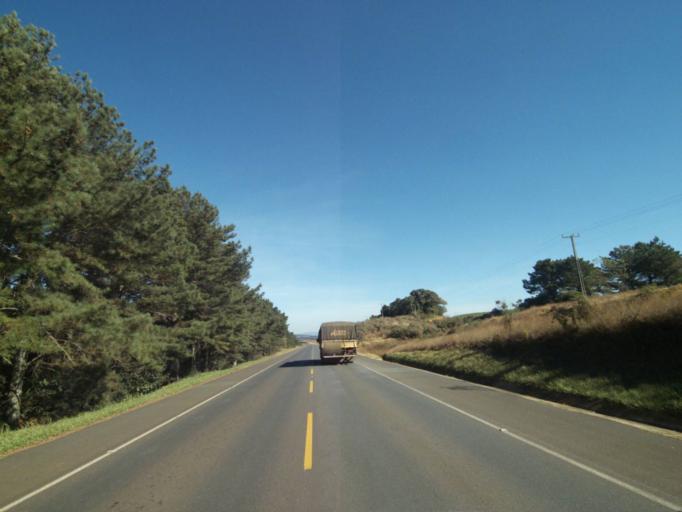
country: BR
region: Parana
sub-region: Tibagi
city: Tibagi
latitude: -24.3653
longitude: -50.3235
